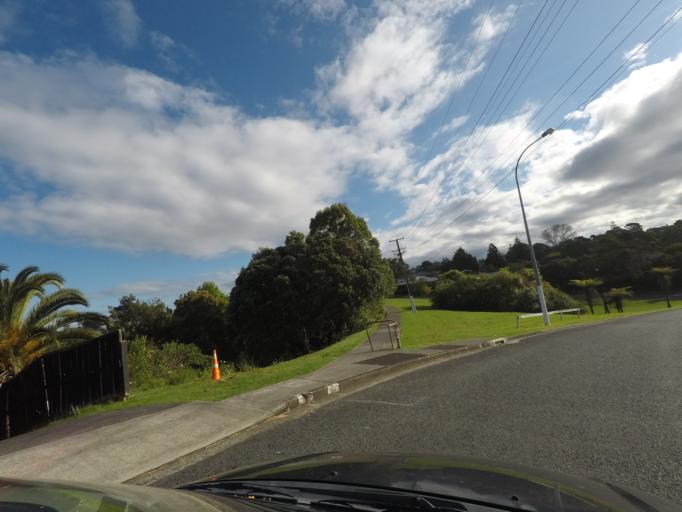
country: NZ
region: Auckland
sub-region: Auckland
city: Rosebank
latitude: -36.8817
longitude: 174.6527
